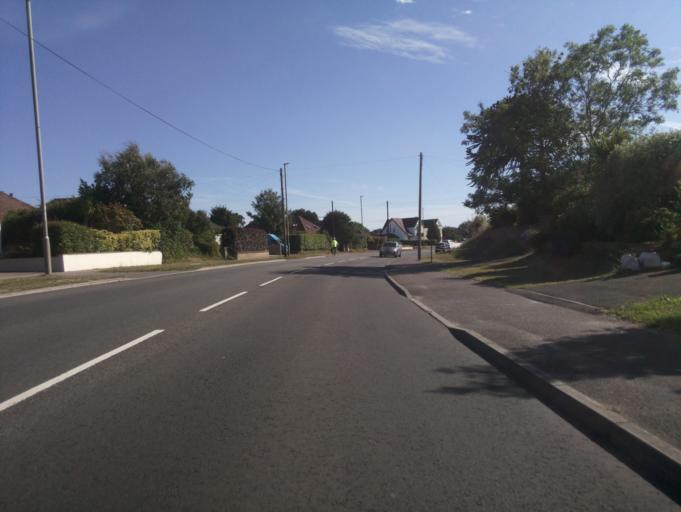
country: GB
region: England
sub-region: Dorset
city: Ferndown
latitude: 50.7764
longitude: -1.8824
